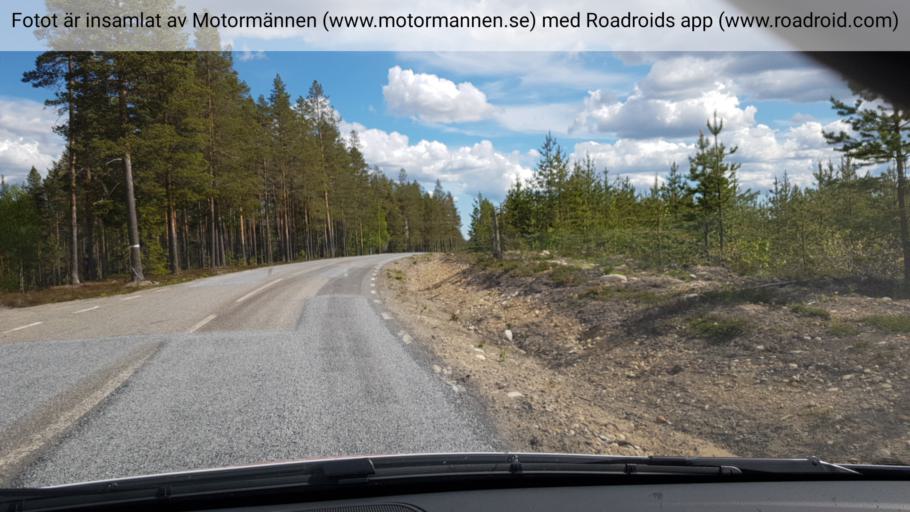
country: SE
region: Vaesterbotten
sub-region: Umea Kommun
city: Ersmark
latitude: 64.2159
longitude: 20.3103
